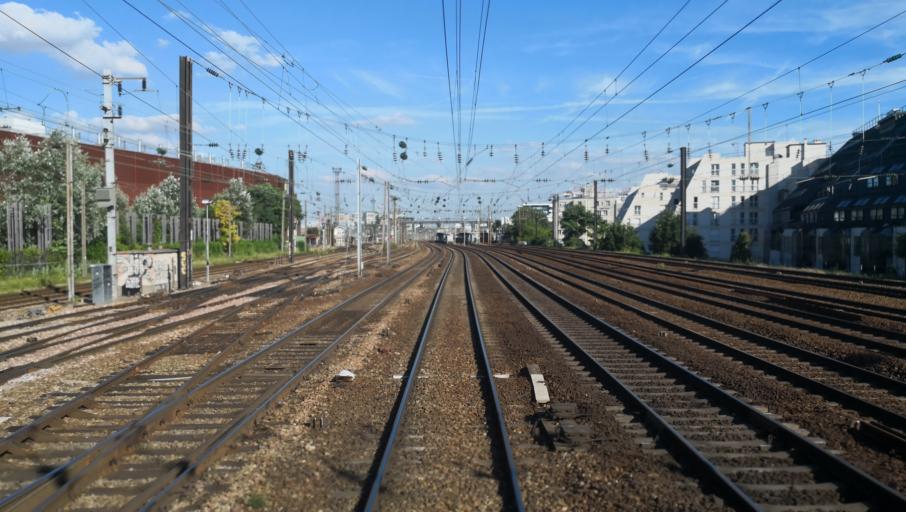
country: FR
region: Ile-de-France
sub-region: Departement des Hauts-de-Seine
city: Levallois-Perret
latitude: 48.9002
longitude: 2.2935
